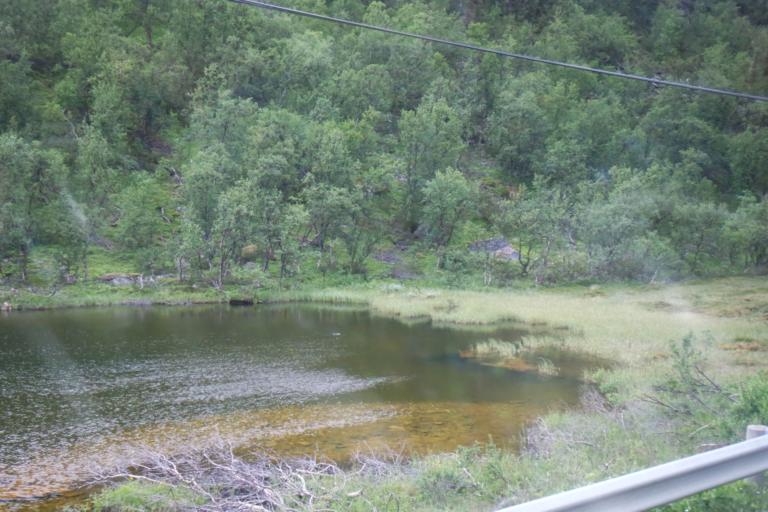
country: NO
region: Finnmark Fylke
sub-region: Porsanger
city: Lakselv
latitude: 70.2759
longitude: 25.0643
